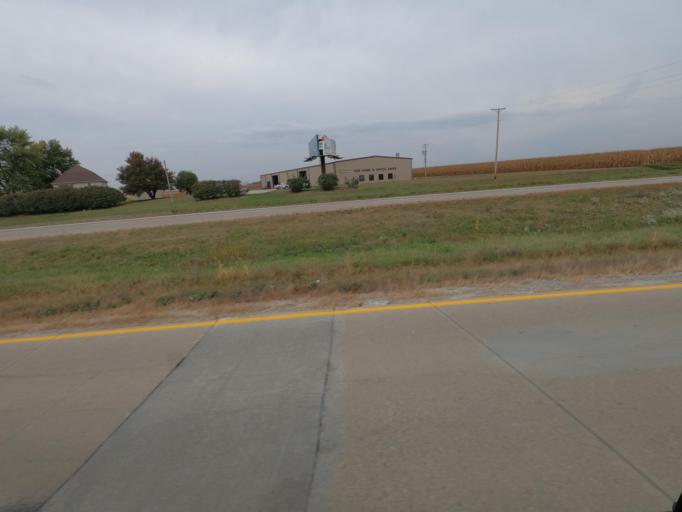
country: US
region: Iowa
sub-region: Marion County
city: Pella
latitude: 41.3756
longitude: -92.8128
